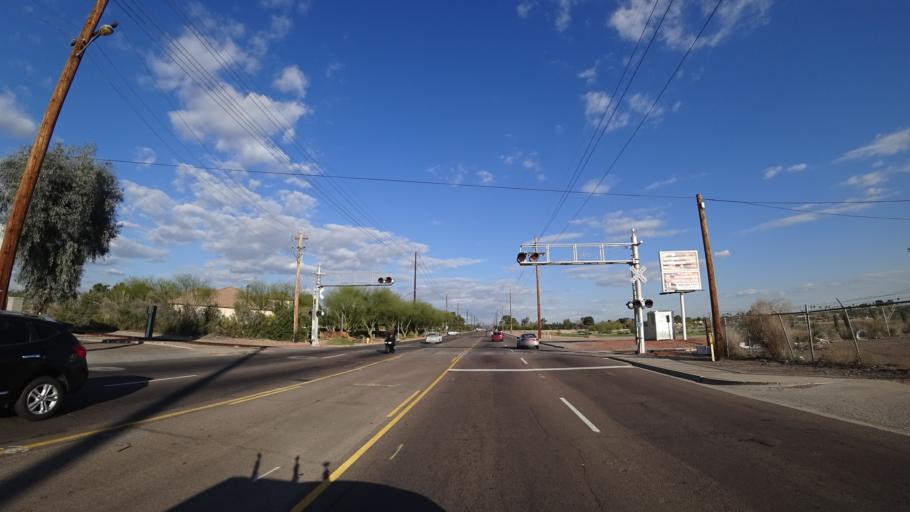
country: US
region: Arizona
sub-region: Maricopa County
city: Glendale
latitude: 33.5528
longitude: -112.1997
